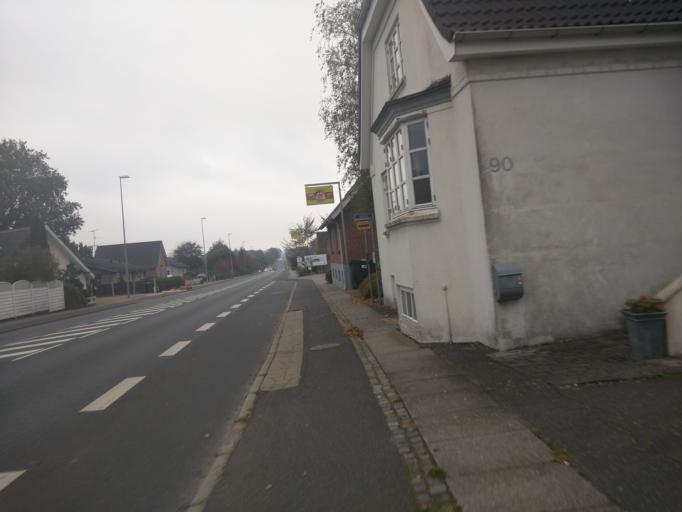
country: DK
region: Central Jutland
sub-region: Silkeborg Kommune
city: Silkeborg
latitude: 56.2130
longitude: 9.5025
